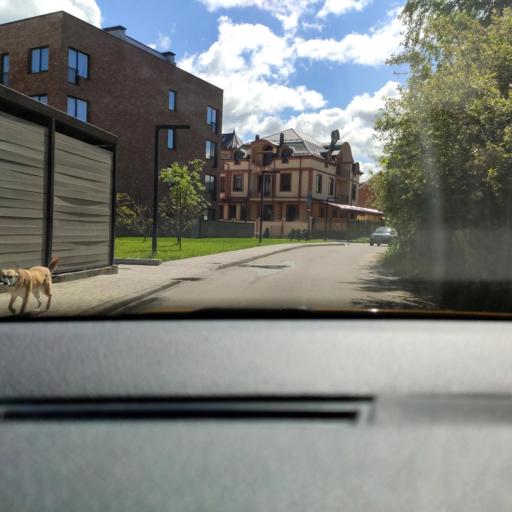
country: RU
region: Moskovskaya
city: Dzerzhinskiy
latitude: 55.6525
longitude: 37.8684
